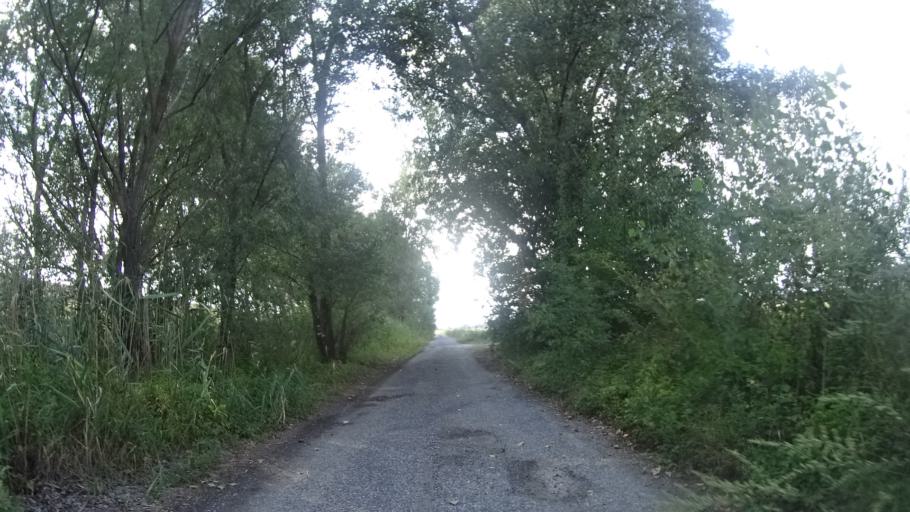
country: HU
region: Gyor-Moson-Sopron
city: Asvanyraro
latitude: 47.9288
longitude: 17.4752
